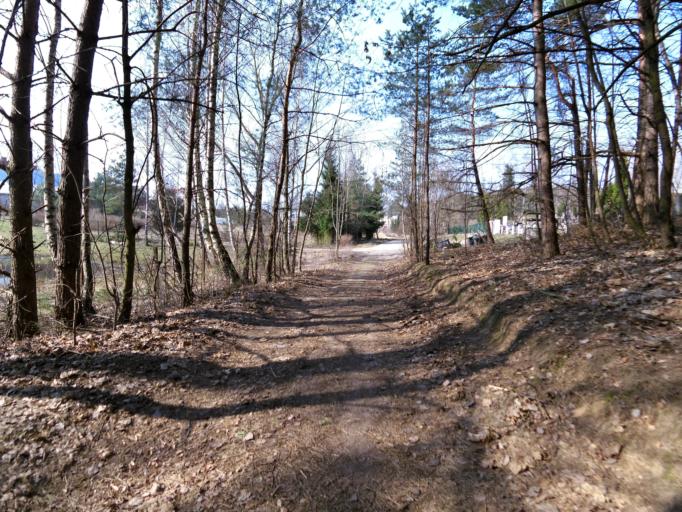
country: LT
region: Vilnius County
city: Pilaite
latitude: 54.6952
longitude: 25.1688
